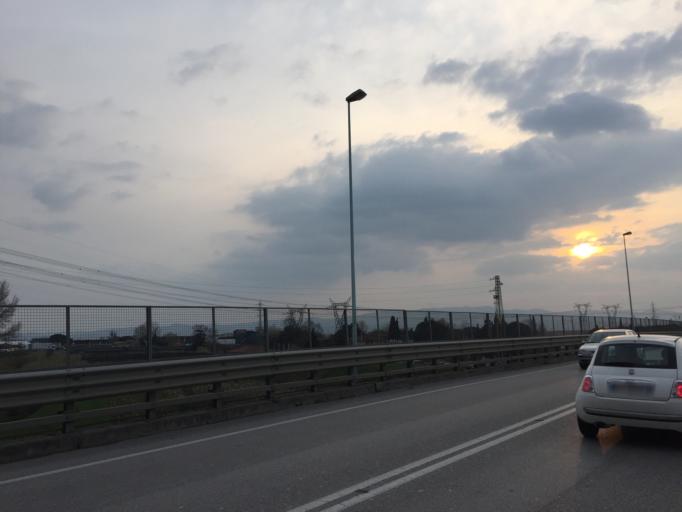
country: IT
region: Tuscany
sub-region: Province of Florence
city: Campi Bisenzio
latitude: 43.8535
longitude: 11.1254
